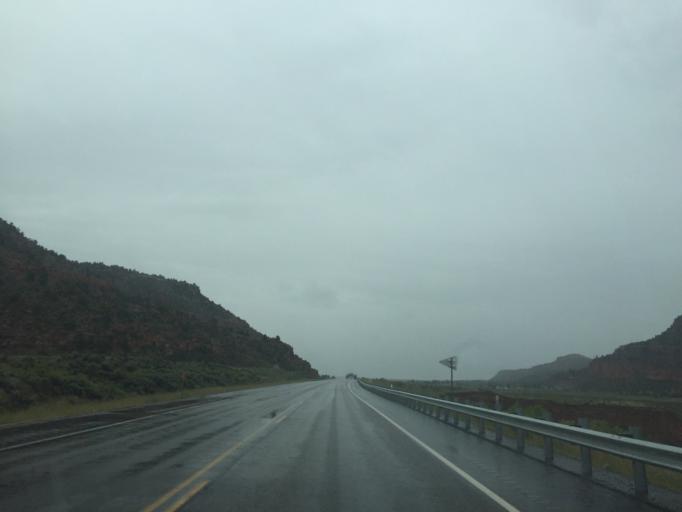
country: US
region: Utah
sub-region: Kane County
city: Kanab
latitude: 37.0701
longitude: -112.5368
